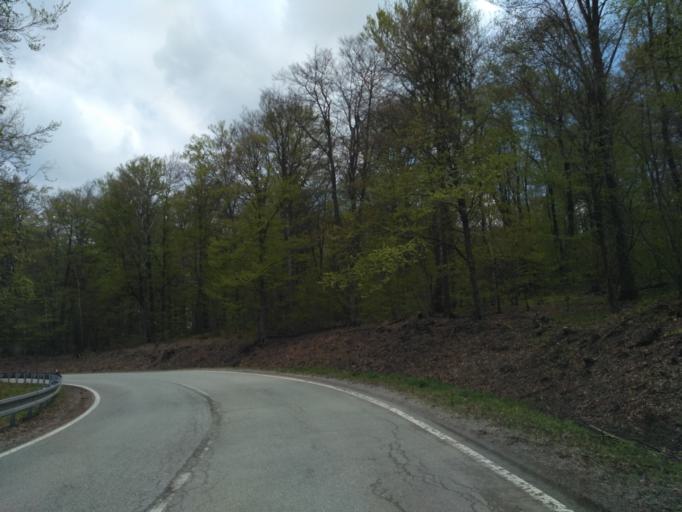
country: SK
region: Kosicky
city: Kosice
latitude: 48.7701
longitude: 21.1404
